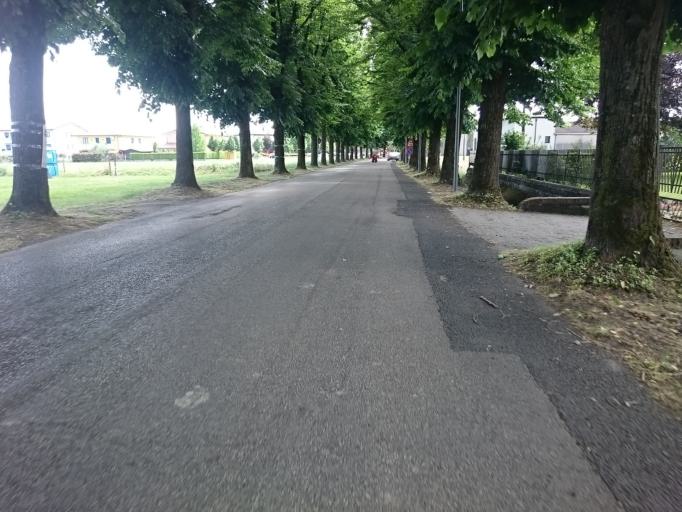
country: IT
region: Veneto
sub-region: Provincia di Padova
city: Carceri
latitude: 45.1976
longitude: 11.6235
